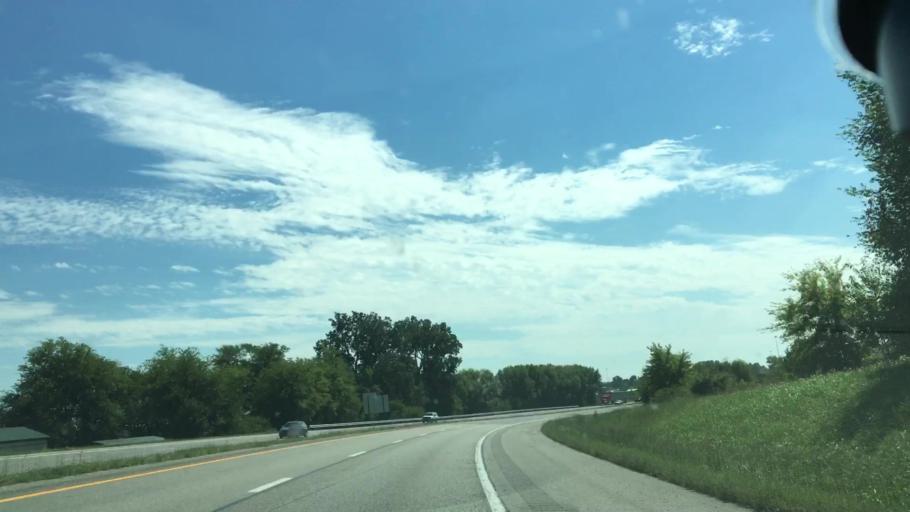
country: US
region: Kentucky
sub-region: Henderson County
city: Henderson
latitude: 37.8222
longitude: -87.5633
